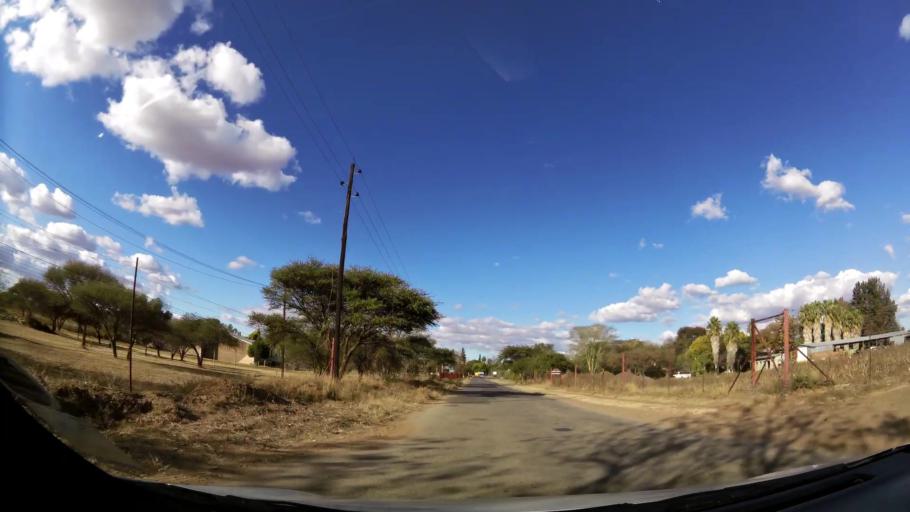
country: ZA
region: Limpopo
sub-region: Capricorn District Municipality
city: Polokwane
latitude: -23.9299
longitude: 29.4474
